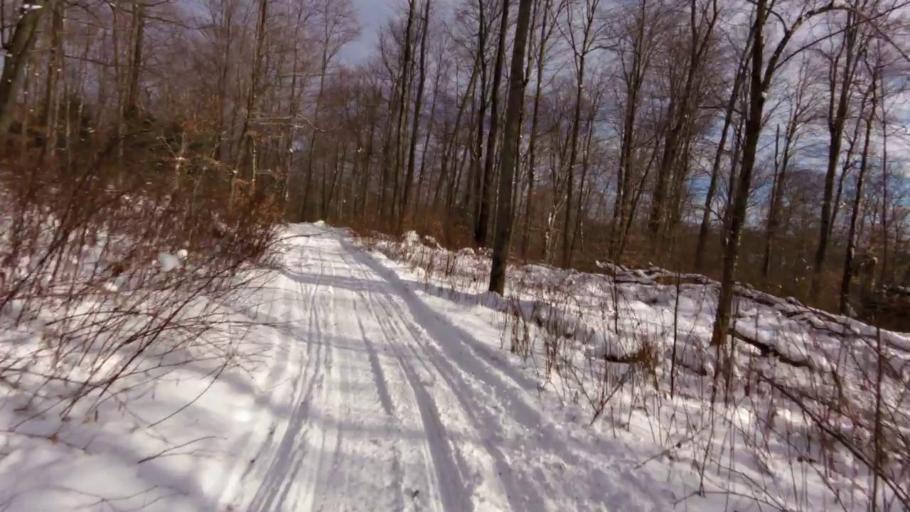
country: US
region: Pennsylvania
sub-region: McKean County
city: Foster Brook
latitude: 41.9994
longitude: -78.5406
